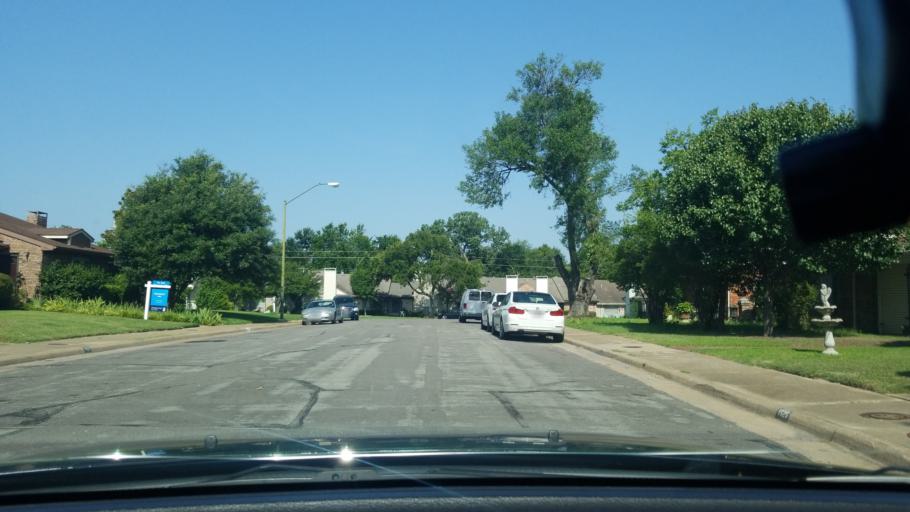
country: US
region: Texas
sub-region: Dallas County
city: Mesquite
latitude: 32.8076
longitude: -96.6895
